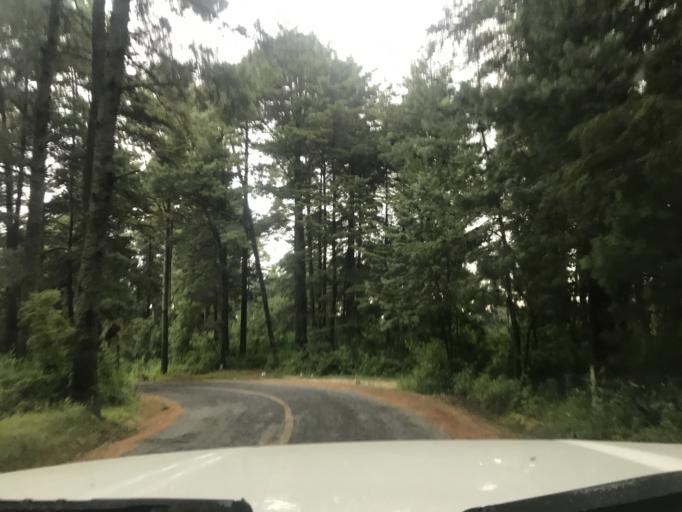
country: MX
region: Morelos
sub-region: Ocuituco
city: Huepalcalco (San Miguel)
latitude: 18.9143
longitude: -98.7516
